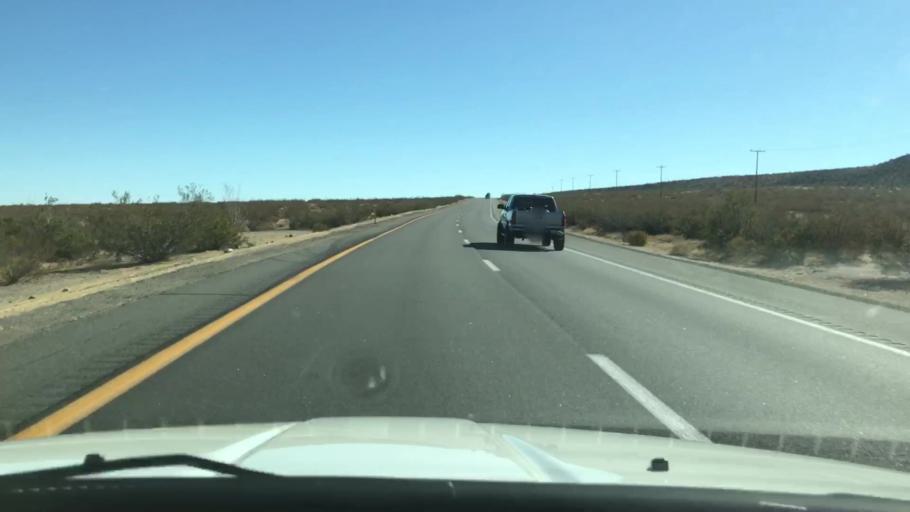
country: US
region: California
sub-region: Kern County
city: Inyokern
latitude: 35.8814
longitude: -117.8910
